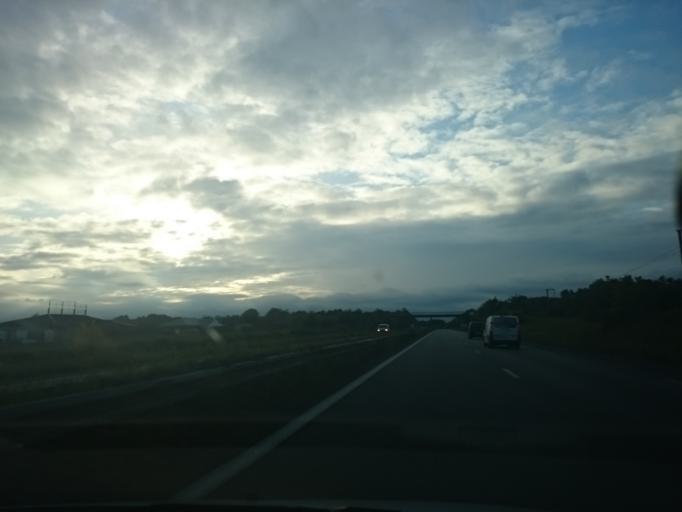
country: FR
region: Brittany
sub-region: Departement du Finistere
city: Redene
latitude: 47.8395
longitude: -3.4938
